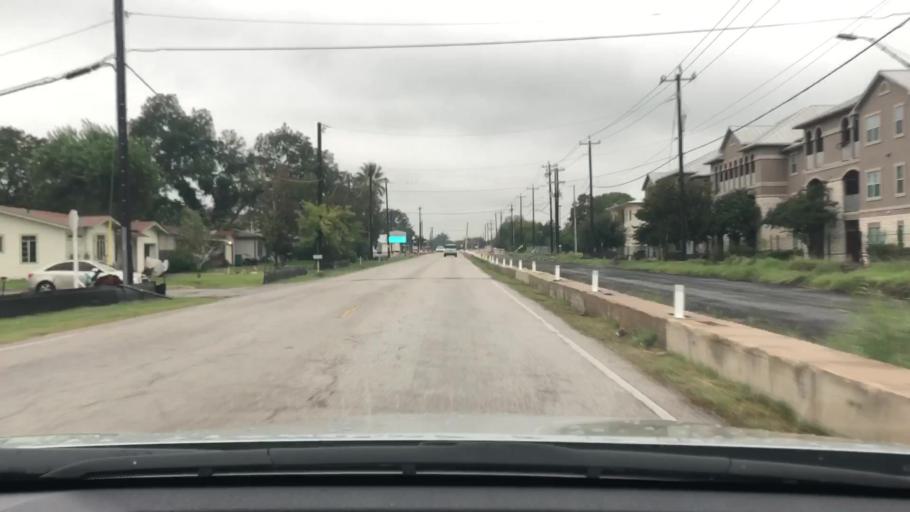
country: US
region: Texas
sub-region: Bexar County
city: Converse
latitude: 29.5136
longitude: -98.3110
